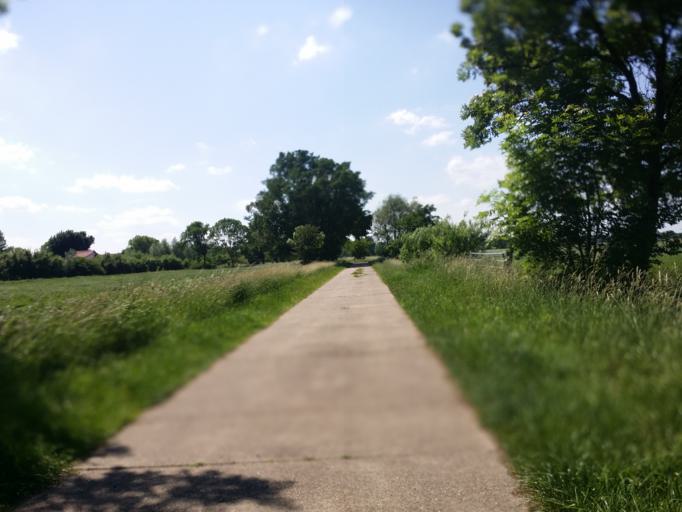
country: DE
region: Lower Saxony
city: Lemwerder
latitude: 53.1431
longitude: 8.5883
